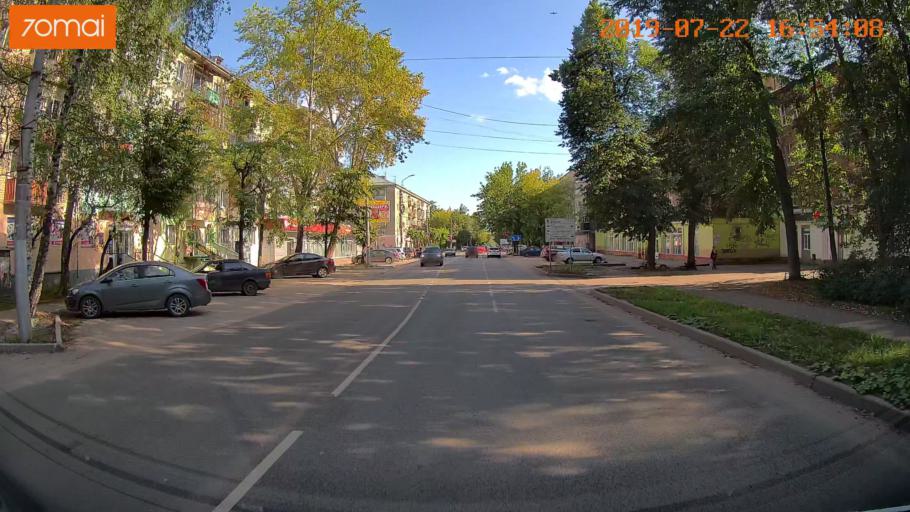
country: RU
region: Ivanovo
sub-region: Gorod Ivanovo
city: Ivanovo
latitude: 57.0120
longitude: 40.9790
